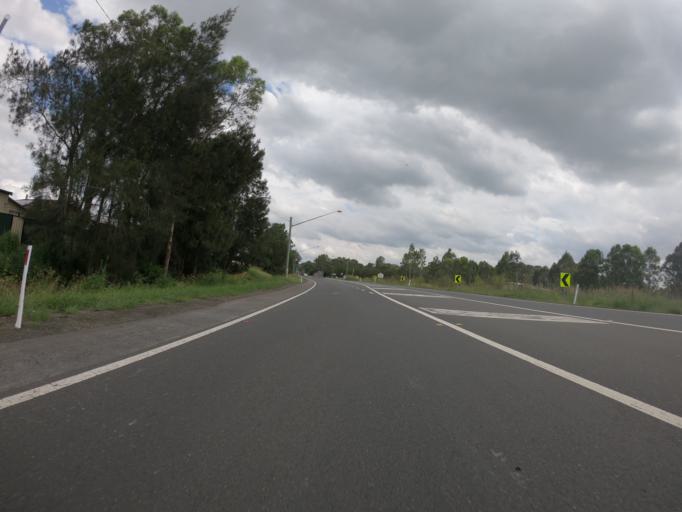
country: AU
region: New South Wales
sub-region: Blacktown
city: Mount Druitt
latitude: -33.8022
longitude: 150.7686
